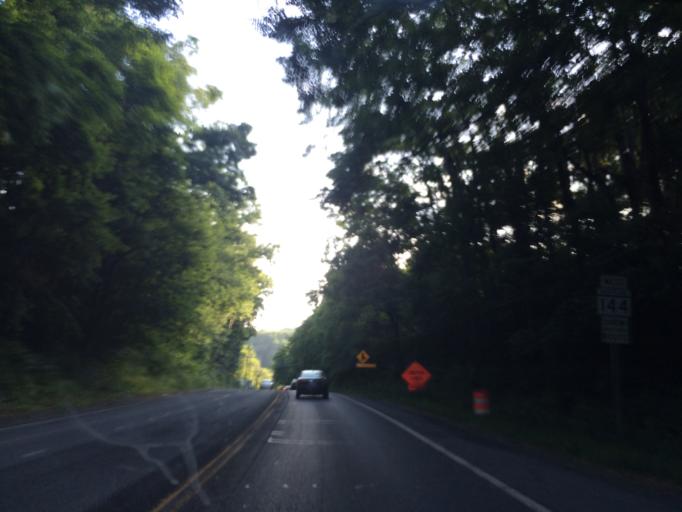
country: US
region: Maryland
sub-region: Howard County
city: Ilchester
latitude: 39.2646
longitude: -76.7778
